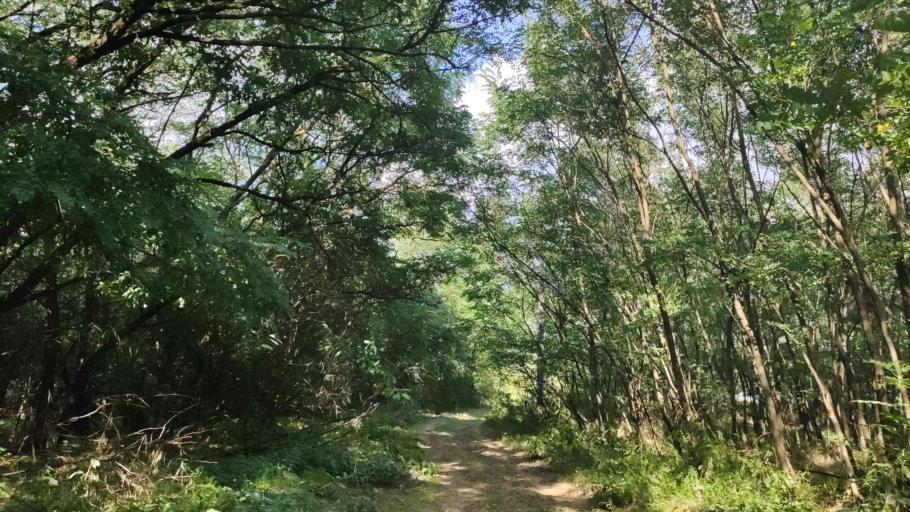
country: HU
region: Pest
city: Biatorbagy
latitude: 47.4659
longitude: 18.8610
